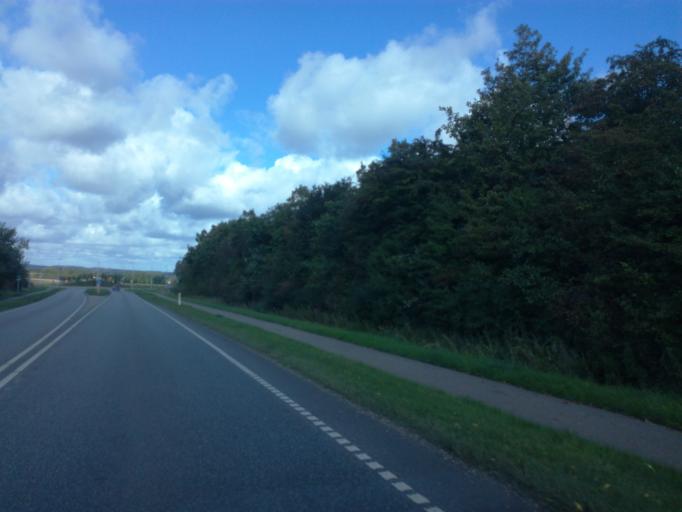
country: DK
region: South Denmark
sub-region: Fredericia Kommune
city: Fredericia
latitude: 55.6064
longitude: 9.7573
